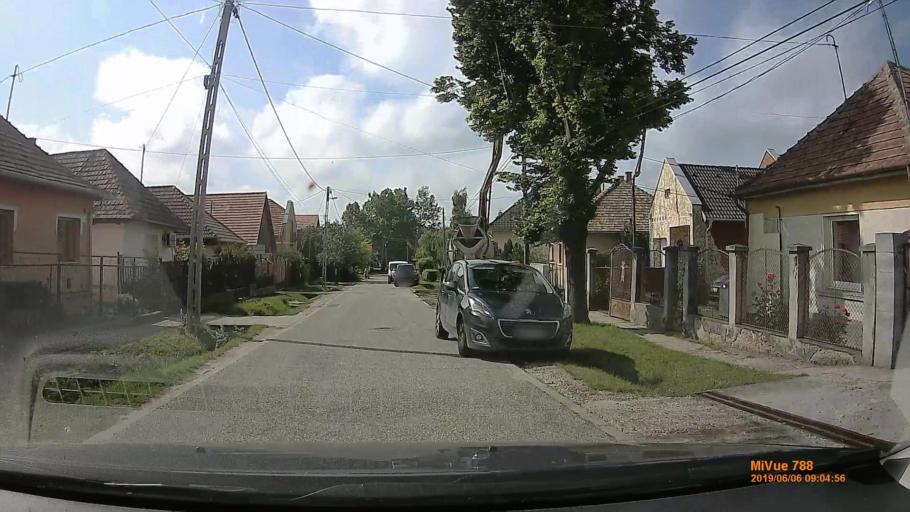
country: HU
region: Pest
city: Maglod
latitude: 47.4443
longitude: 19.3479
